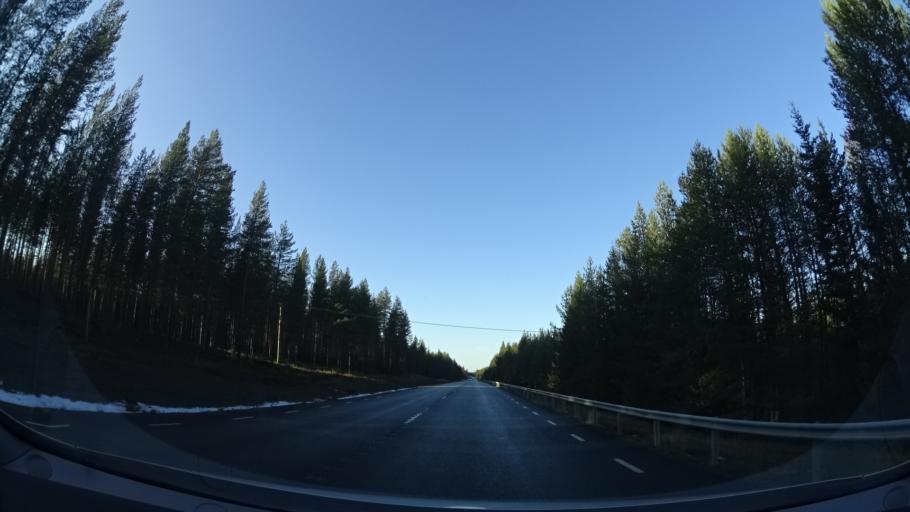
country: SE
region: Vaesterbotten
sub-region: Skelleftea Kommun
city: Langsele
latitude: 64.9396
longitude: 19.9373
